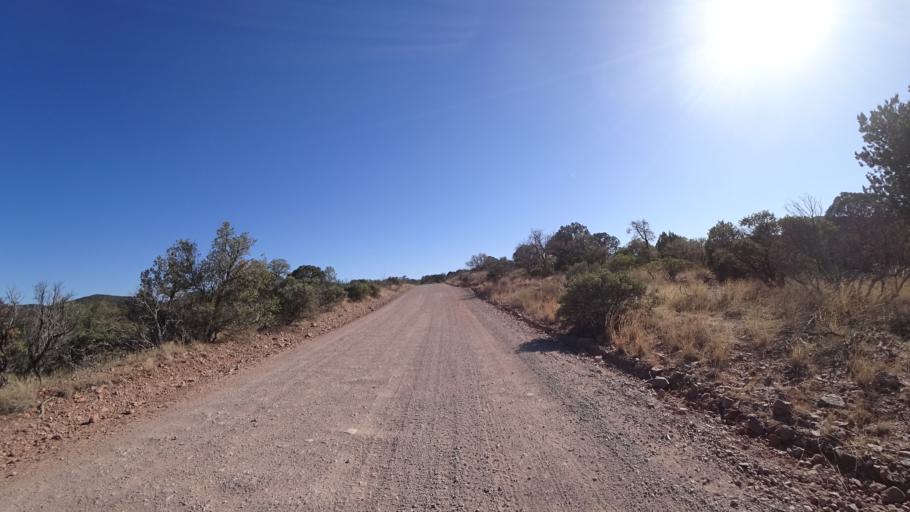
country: US
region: Arizona
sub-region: Cochise County
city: Huachuca City
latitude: 31.5305
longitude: -110.5330
